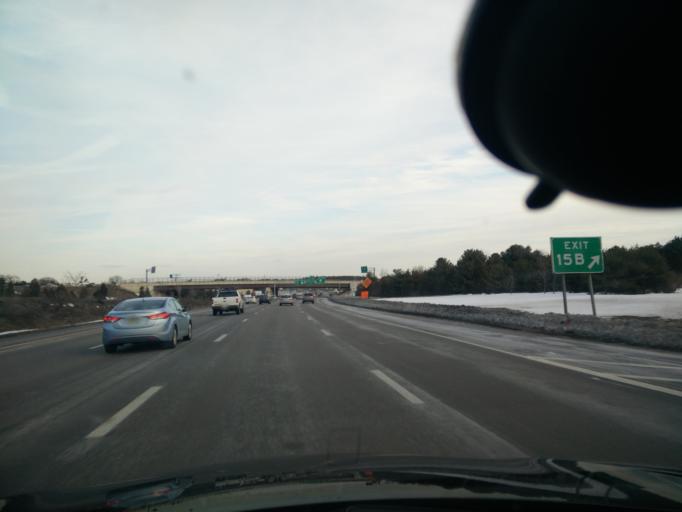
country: US
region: Massachusetts
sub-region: Norfolk County
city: Dedham
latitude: 42.2303
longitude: -71.1844
